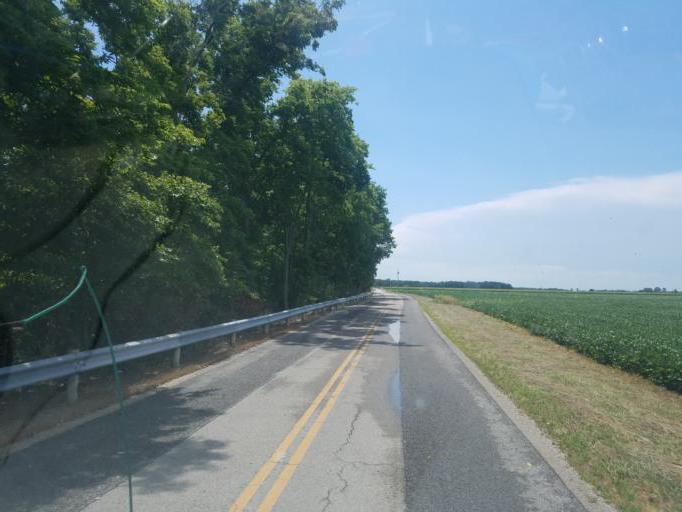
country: US
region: Ohio
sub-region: Paulding County
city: Antwerp
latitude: 41.1896
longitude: -84.7707
